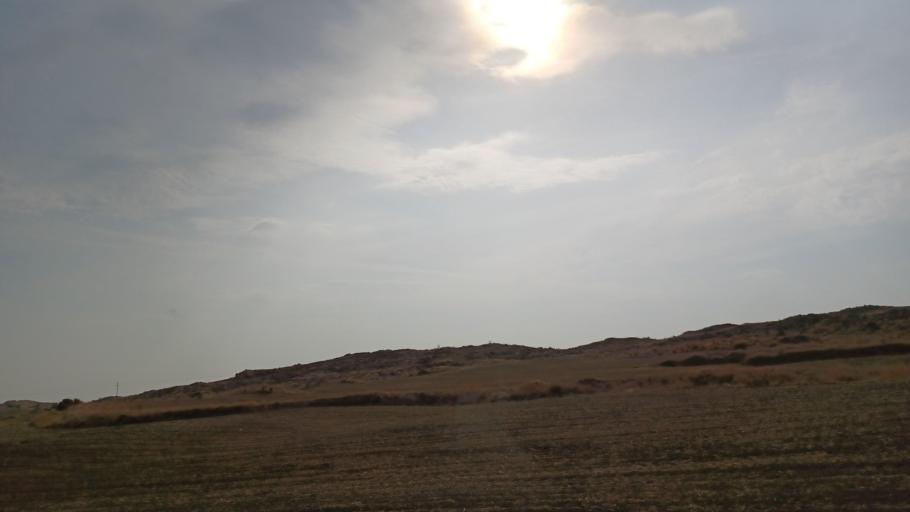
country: CY
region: Larnaka
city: Troulloi
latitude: 35.0146
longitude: 33.5807
